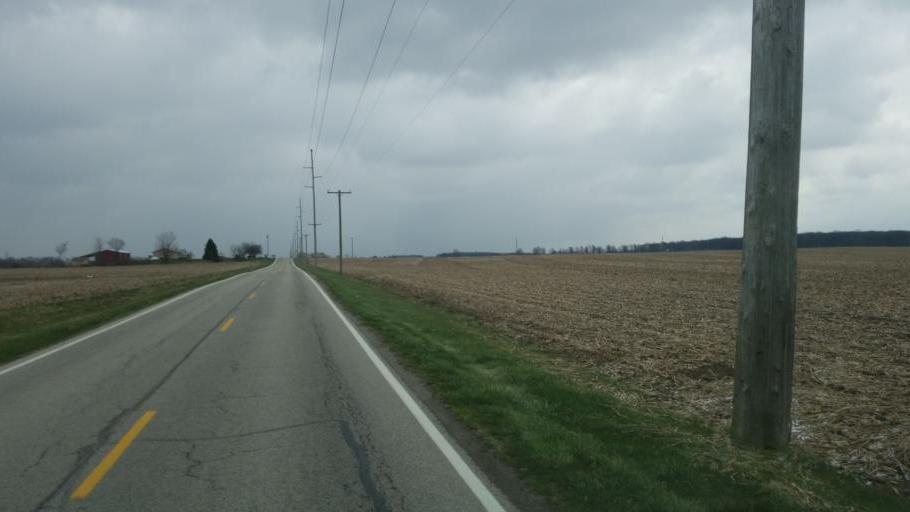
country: US
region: Ohio
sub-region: Union County
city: Richwood
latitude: 40.4512
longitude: -83.3702
